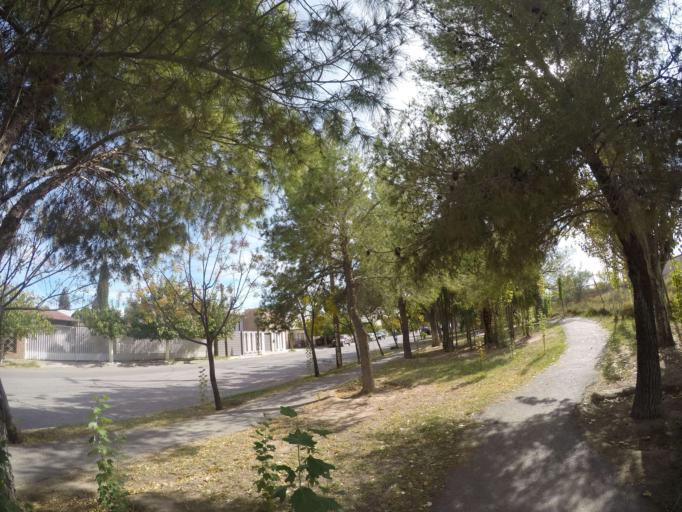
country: MX
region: Chihuahua
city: Ciudad Juarez
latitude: 31.7341
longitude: -106.4354
